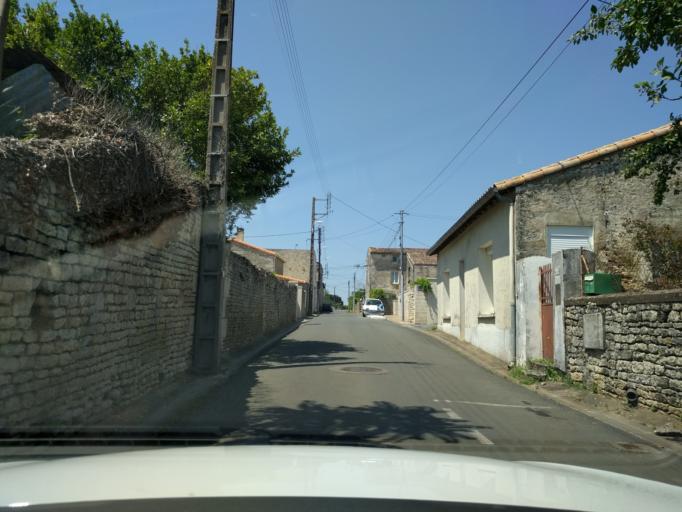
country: FR
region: Poitou-Charentes
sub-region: Departement des Deux-Sevres
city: Niort
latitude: 46.3510
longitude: -0.4713
